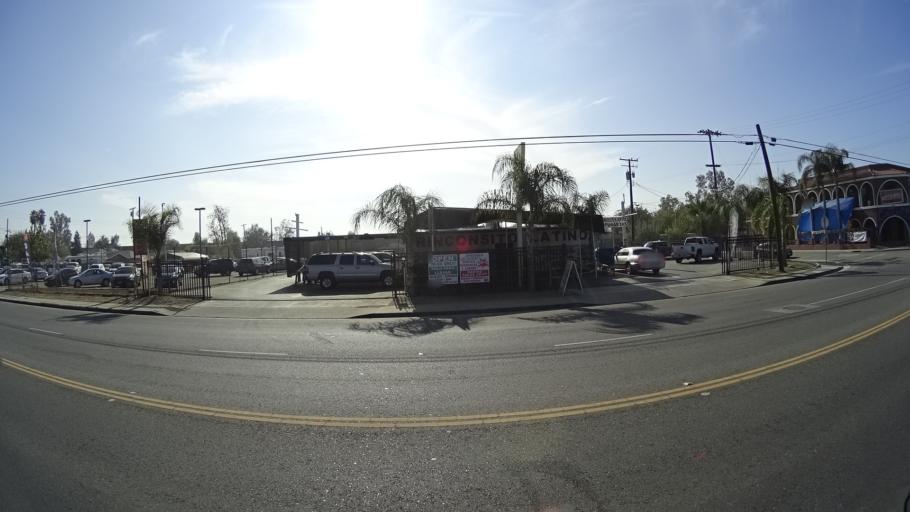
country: US
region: California
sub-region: Kern County
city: Bakersfield
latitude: 35.3537
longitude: -118.9967
